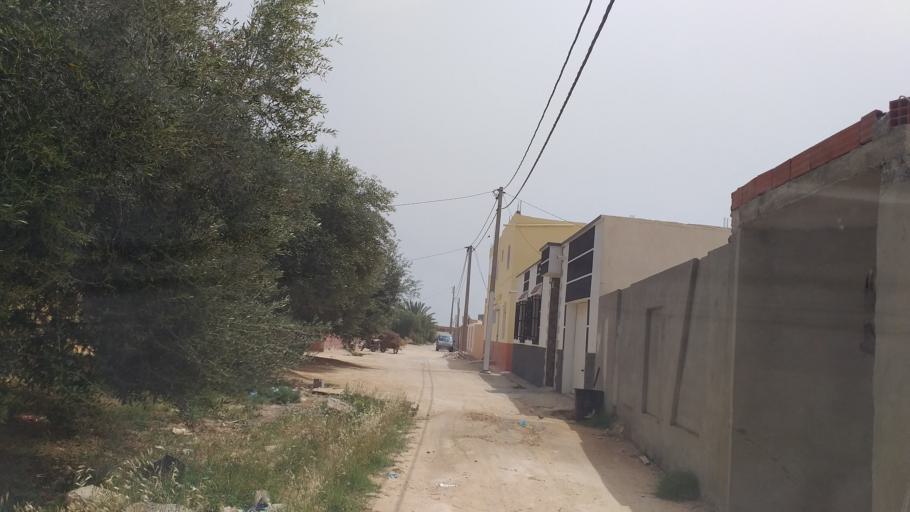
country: TN
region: Qabis
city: Gabes
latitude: 33.9518
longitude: 10.0652
